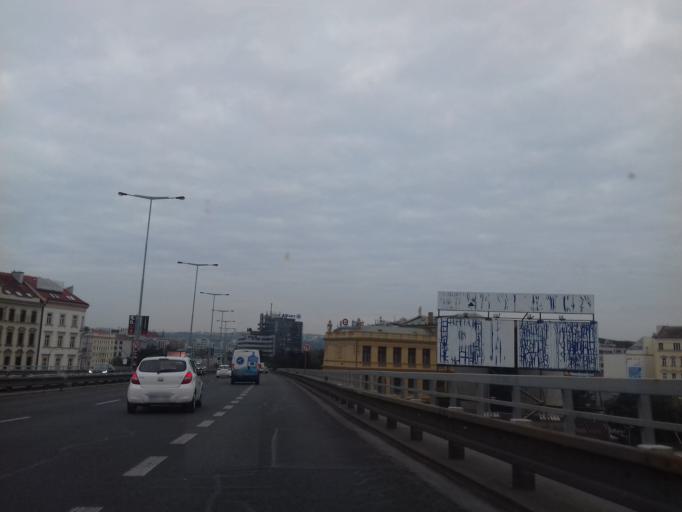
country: CZ
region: Praha
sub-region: Praha 8
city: Karlin
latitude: 50.0886
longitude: 14.4380
